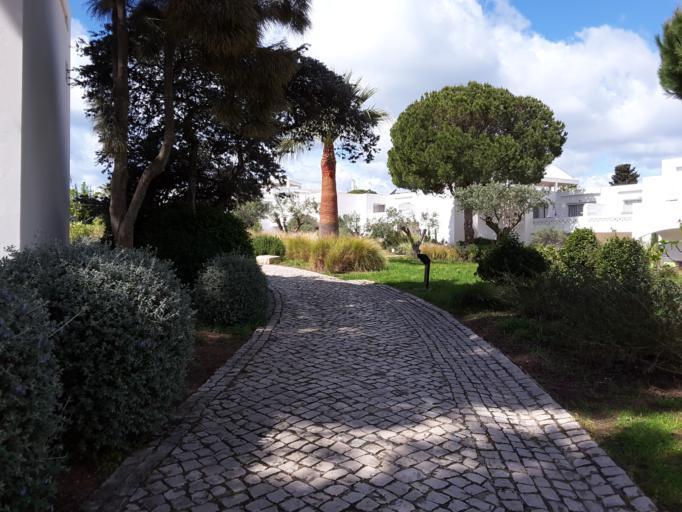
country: PT
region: Faro
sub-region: Albufeira
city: Albufeira
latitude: 37.0769
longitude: -8.2949
